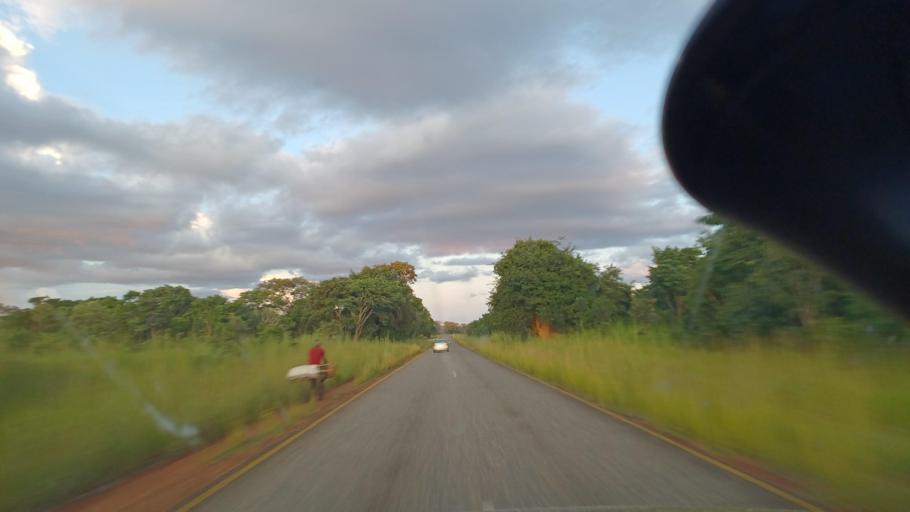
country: ZM
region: North-Western
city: Kasempa
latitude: -12.9979
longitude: 25.6560
